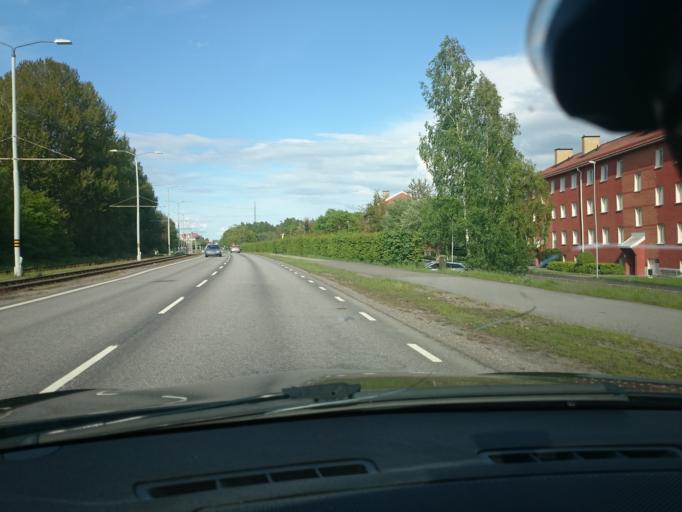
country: SE
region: OEstergoetland
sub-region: Norrkopings Kommun
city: Norrkoping
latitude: 58.5780
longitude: 16.1511
